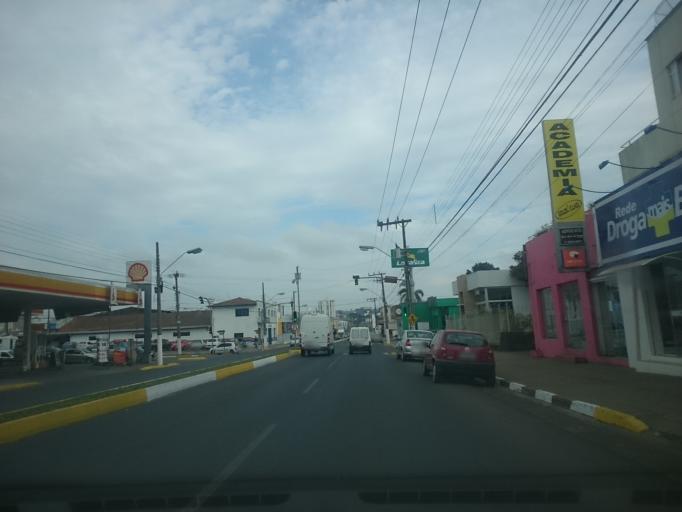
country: BR
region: Santa Catarina
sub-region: Lages
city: Lages
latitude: -27.8114
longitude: -50.3130
